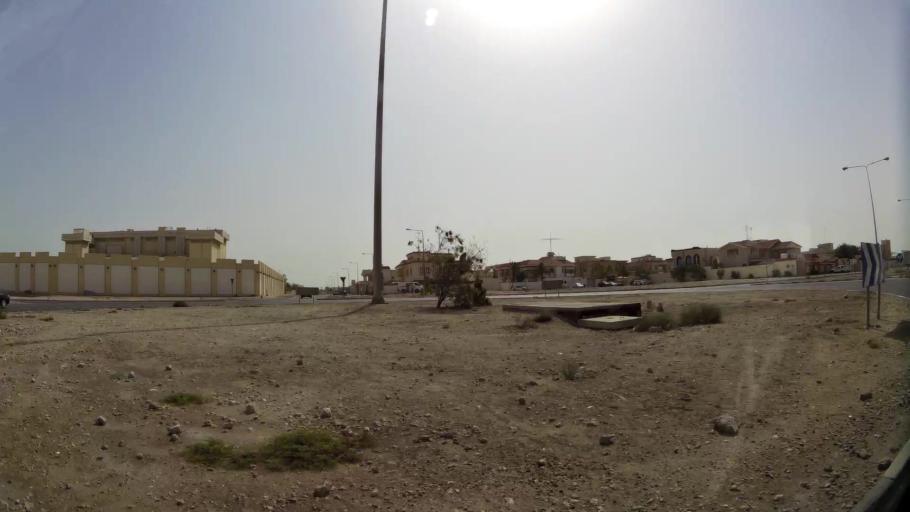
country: QA
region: Baladiyat ad Dawhah
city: Doha
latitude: 25.2462
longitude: 51.5241
